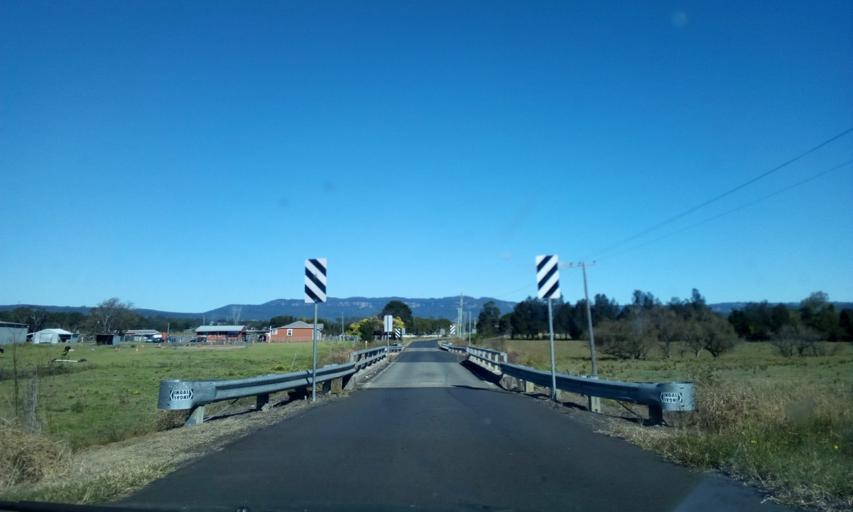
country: AU
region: New South Wales
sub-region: Wollongong
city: Dapto
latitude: -34.5261
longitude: 150.7772
